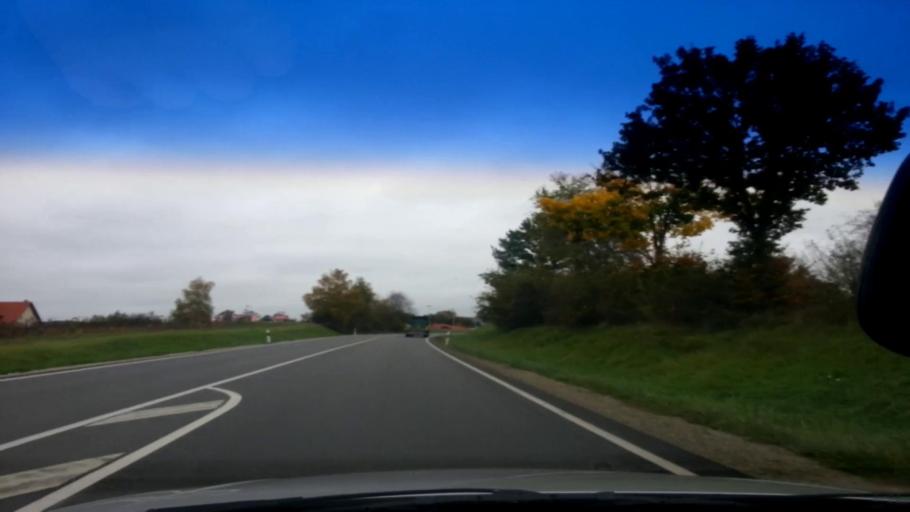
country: DE
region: Bavaria
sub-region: Upper Franconia
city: Stegaurach
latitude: 49.8623
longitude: 10.8596
